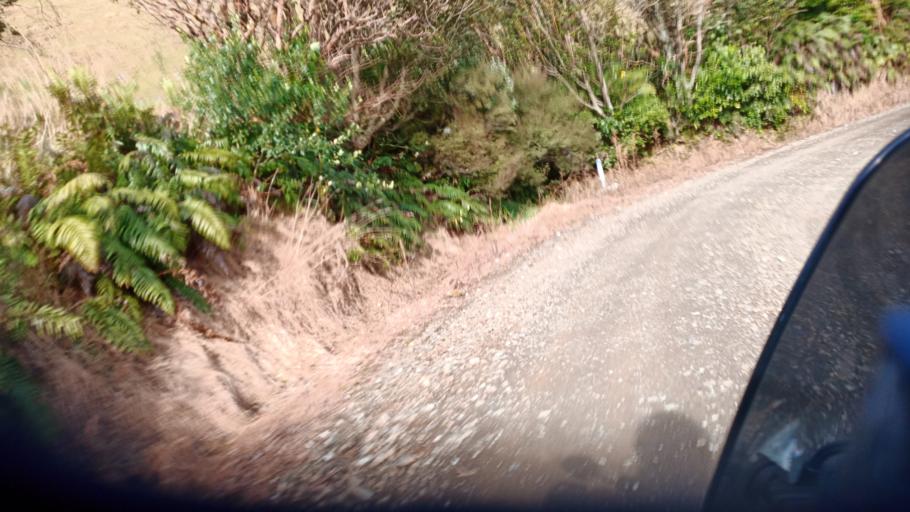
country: NZ
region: Gisborne
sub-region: Gisborne District
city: Gisborne
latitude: -38.4547
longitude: 177.5392
